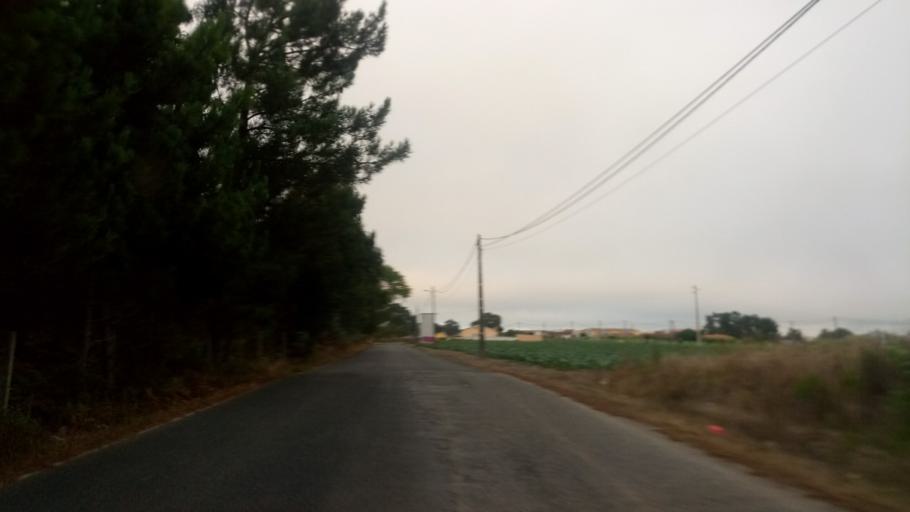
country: PT
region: Leiria
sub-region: Caldas da Rainha
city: Caldas da Rainha
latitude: 39.4212
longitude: -9.1486
